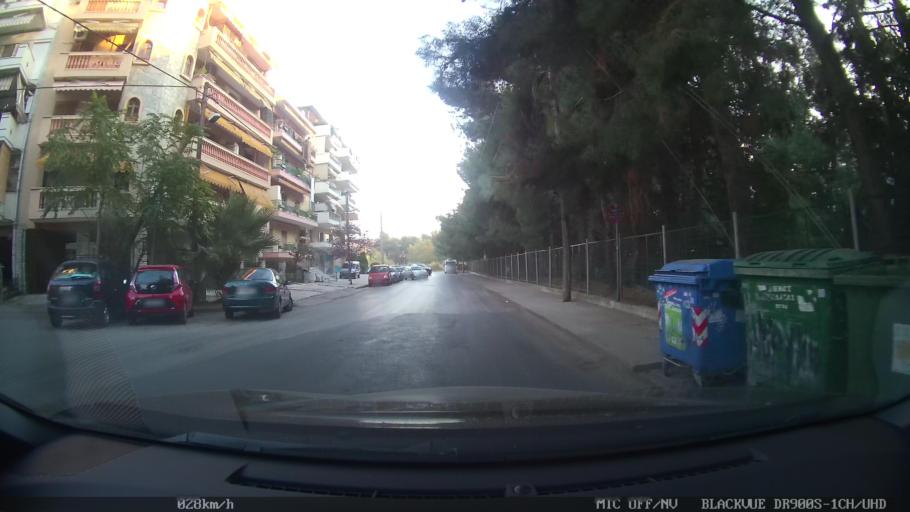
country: GR
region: Central Macedonia
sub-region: Nomos Thessalonikis
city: Pylaia
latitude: 40.6059
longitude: 22.9834
